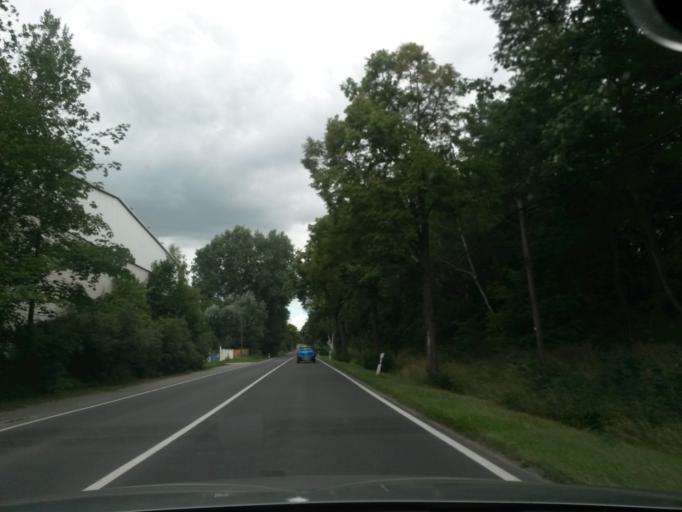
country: DE
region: Brandenburg
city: Angermunde
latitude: 52.9919
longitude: 13.9818
